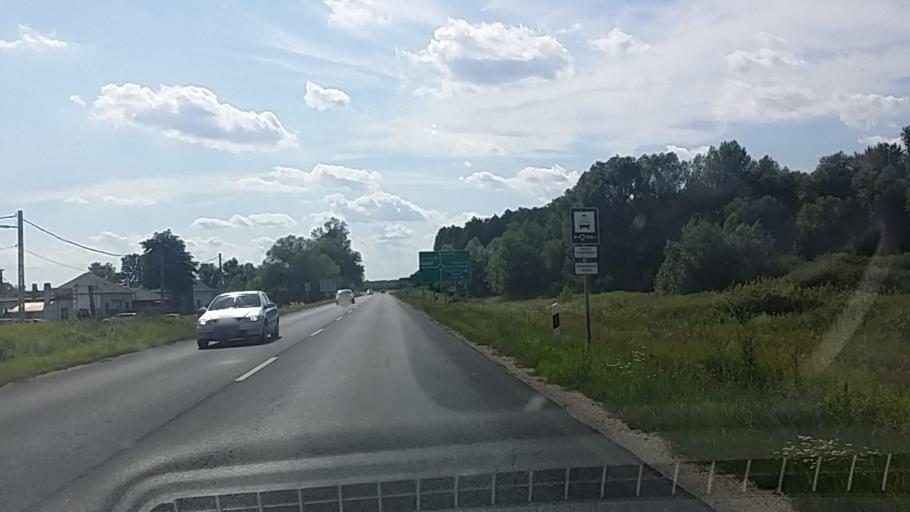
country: HU
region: Zala
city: Nagykanizsa
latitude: 46.4670
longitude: 16.9743
